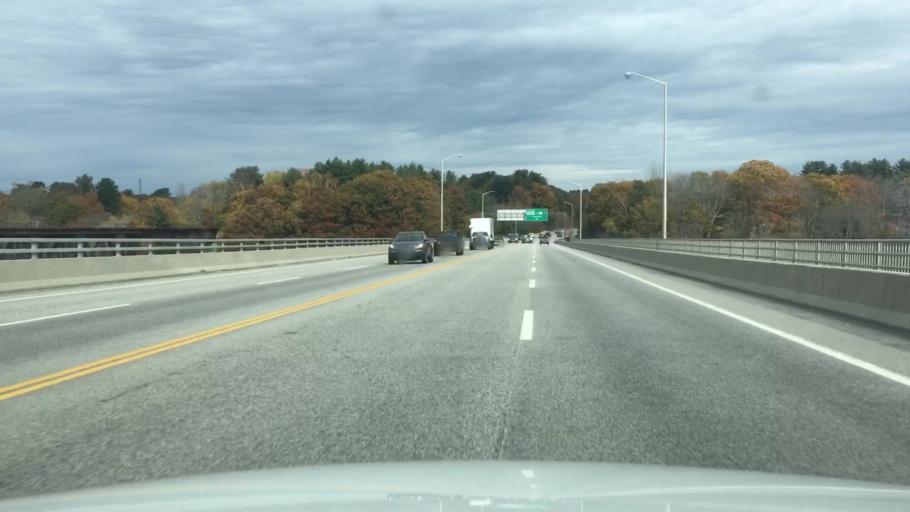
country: US
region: Maine
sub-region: Cumberland County
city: Brunswick
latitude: 43.9219
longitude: -69.9528
